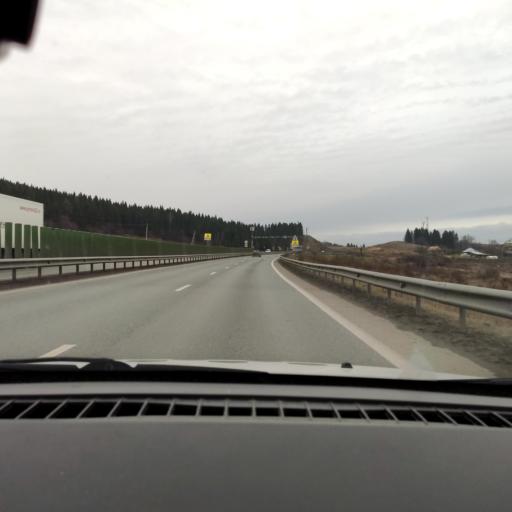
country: RU
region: Perm
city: Froly
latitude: 57.9344
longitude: 56.2101
